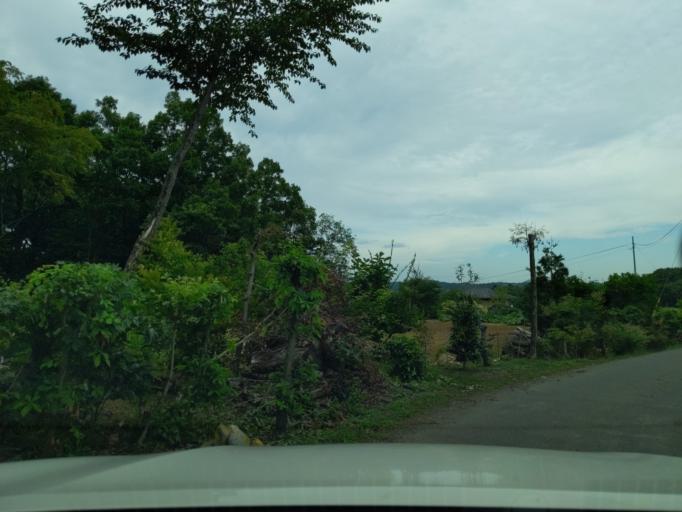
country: JP
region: Fukushima
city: Koriyama
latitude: 37.4345
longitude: 140.4048
